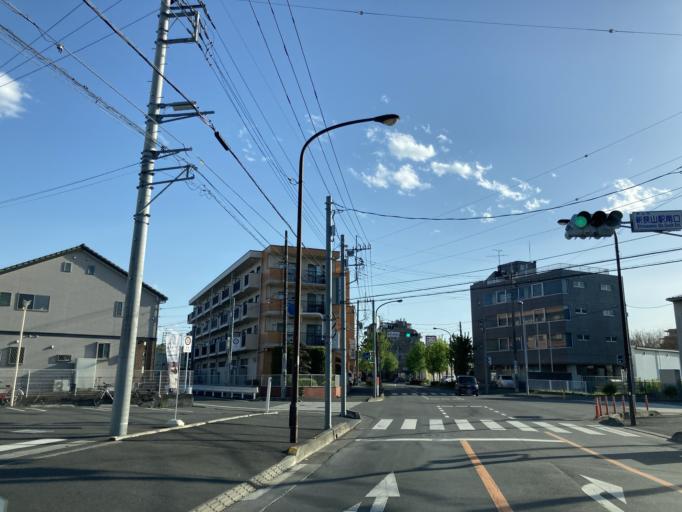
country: JP
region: Saitama
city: Sayama
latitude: 35.8710
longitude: 139.4365
